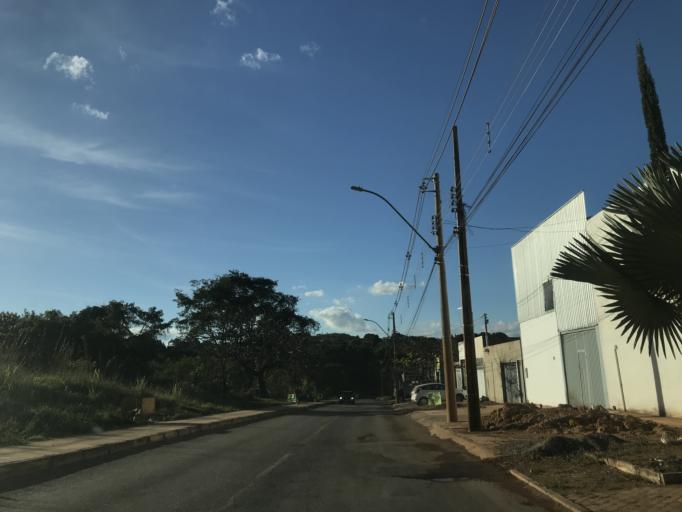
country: BR
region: Federal District
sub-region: Brasilia
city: Brasilia
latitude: -15.8834
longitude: -47.7804
